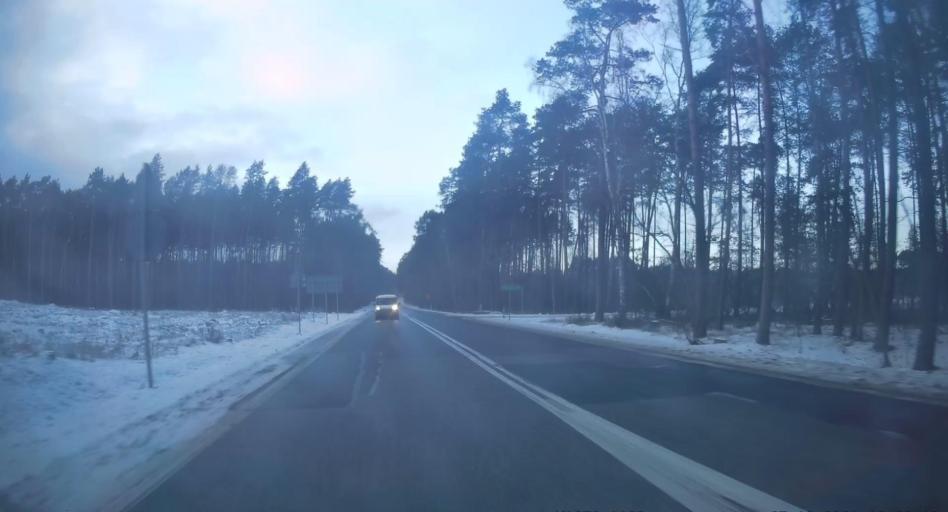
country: PL
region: Swietokrzyskie
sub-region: Powiat konecki
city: Radoszyce
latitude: 51.1032
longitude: 20.3125
